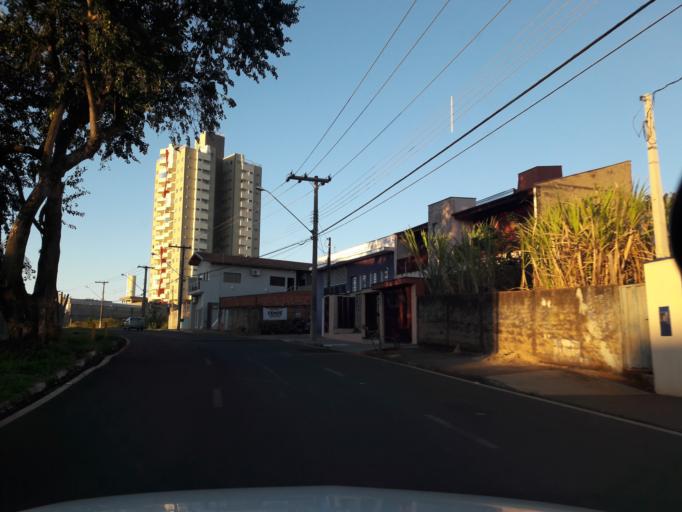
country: BR
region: Sao Paulo
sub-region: Moji-Guacu
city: Mogi-Gaucu
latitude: -22.3658
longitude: -46.9346
